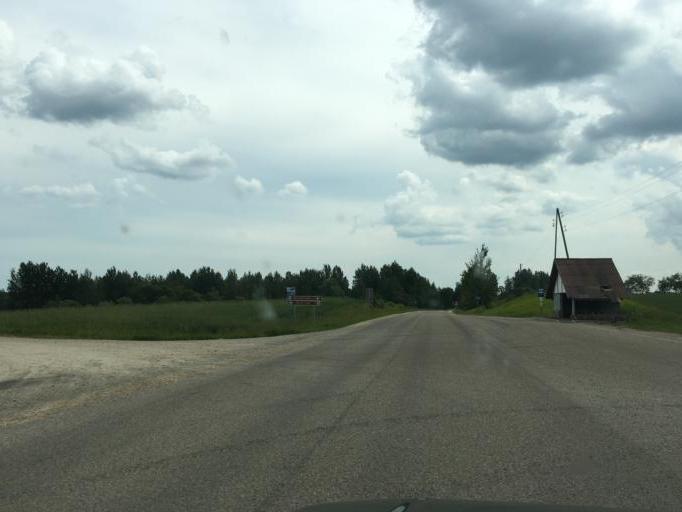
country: LV
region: Rugaju
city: Rugaji
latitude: 56.8474
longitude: 27.0910
